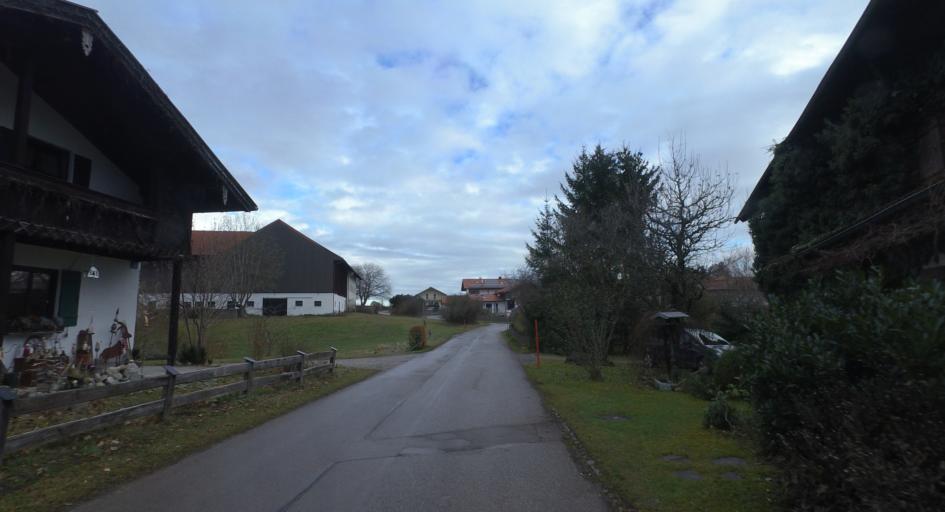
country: DE
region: Bavaria
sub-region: Upper Bavaria
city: Chieming
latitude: 47.9063
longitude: 12.5232
